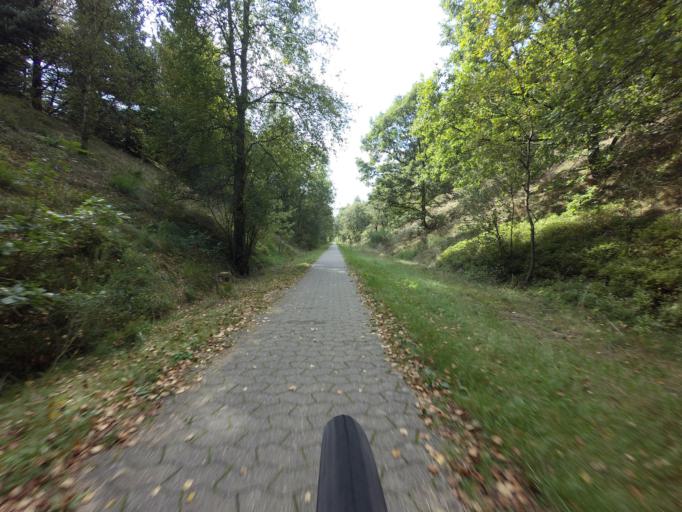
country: DK
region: Central Jutland
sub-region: Viborg Kommune
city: Viborg
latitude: 56.3842
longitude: 9.2945
